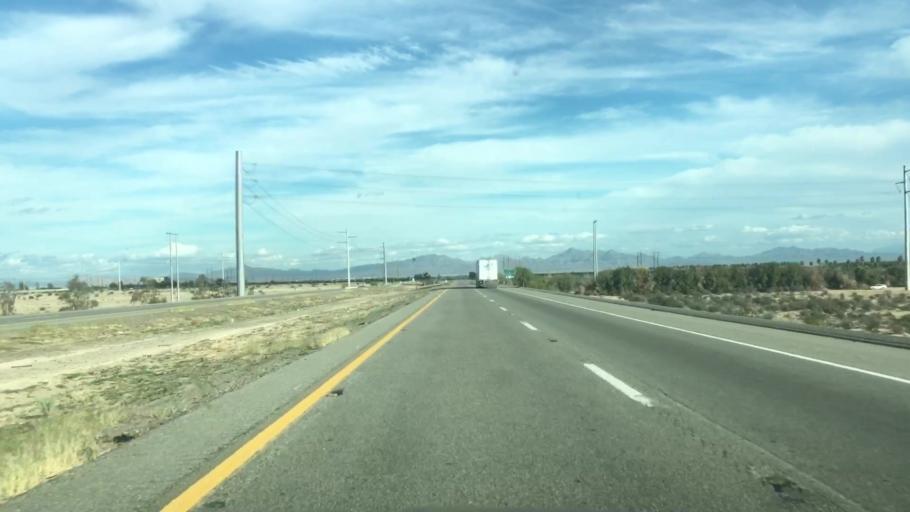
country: US
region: California
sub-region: Riverside County
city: Mesa Verde
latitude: 33.6066
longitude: -114.6992
